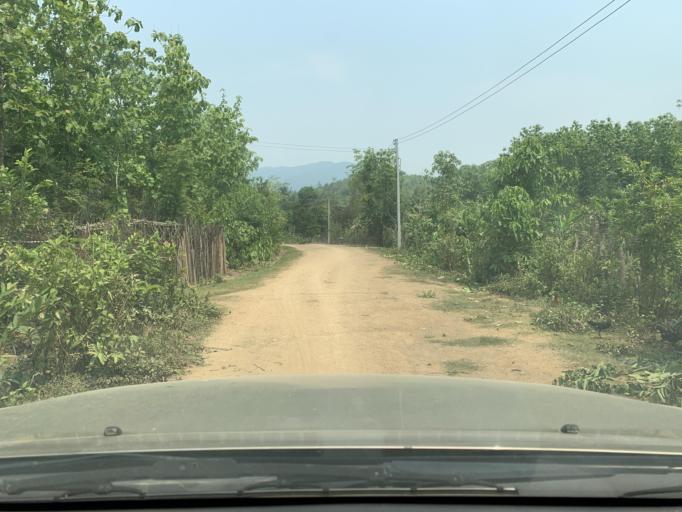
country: LA
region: Louangphabang
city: Louangphabang
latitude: 19.9449
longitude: 102.1341
